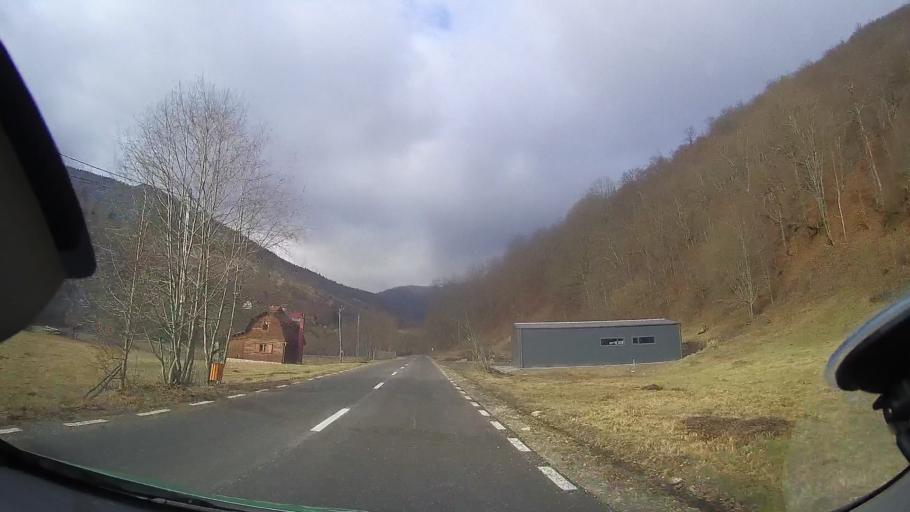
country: RO
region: Cluj
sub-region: Comuna Valea Ierii
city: Valea Ierii
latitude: 46.6392
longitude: 23.3621
